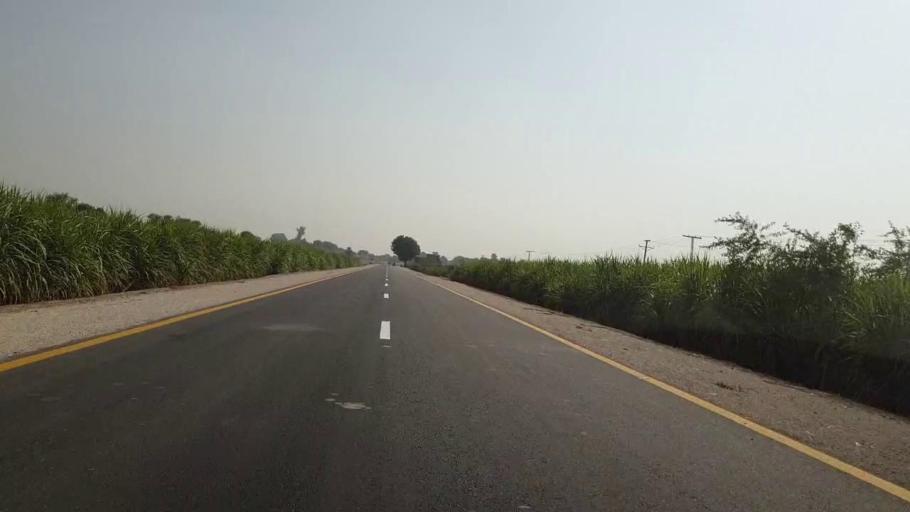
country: PK
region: Sindh
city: Bhan
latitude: 26.6070
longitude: 67.7790
